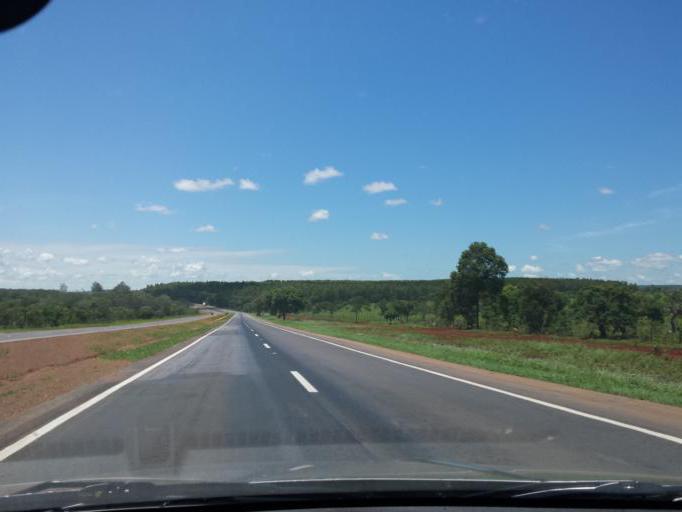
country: BR
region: Goias
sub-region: Luziania
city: Luziania
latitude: -16.4831
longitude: -47.8126
